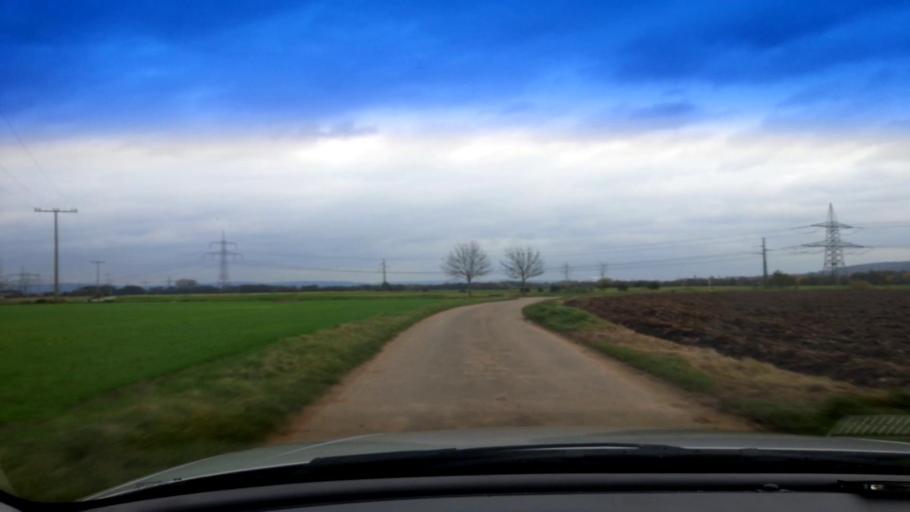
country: DE
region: Bavaria
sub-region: Upper Franconia
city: Oberhaid
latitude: 49.9269
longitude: 10.8203
